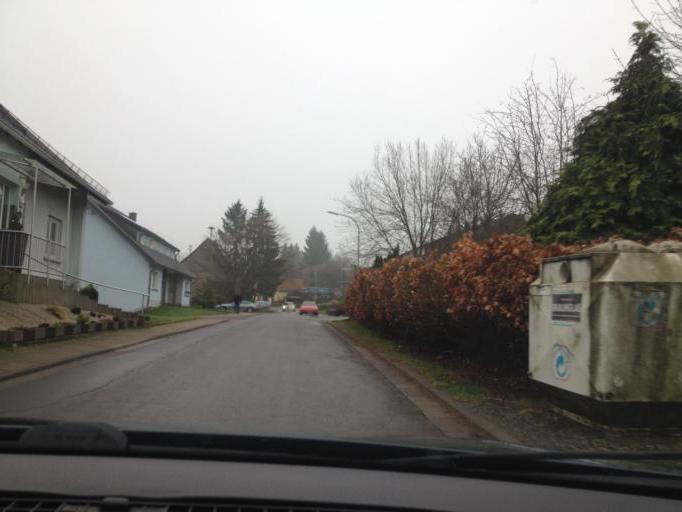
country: DE
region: Saarland
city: Marpingen
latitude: 49.4577
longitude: 7.0914
